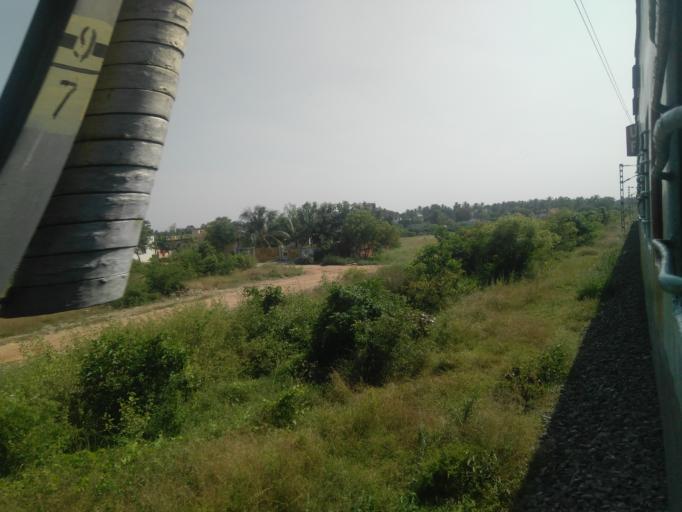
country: IN
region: Tamil Nadu
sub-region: Coimbatore
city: Periyanayakkanpalaiyam
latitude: 11.1007
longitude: 76.9483
